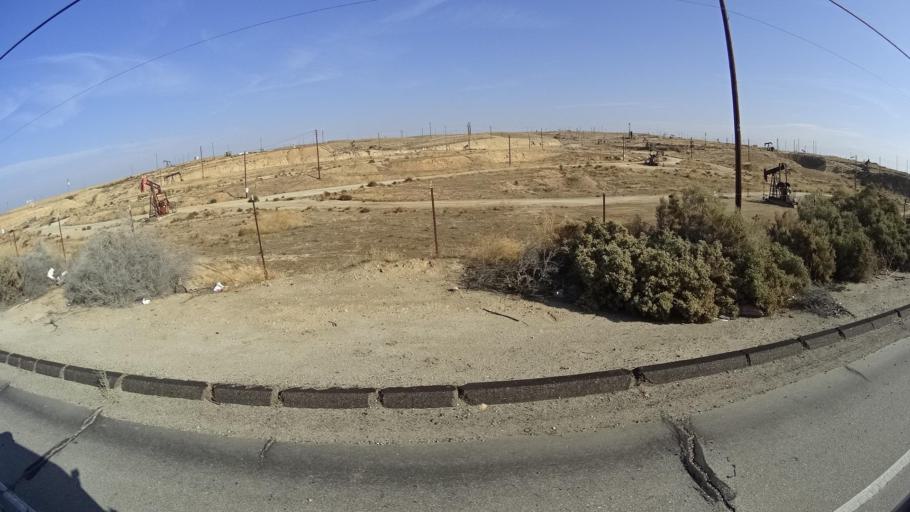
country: US
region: California
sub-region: Kern County
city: Oildale
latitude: 35.4670
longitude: -119.0610
